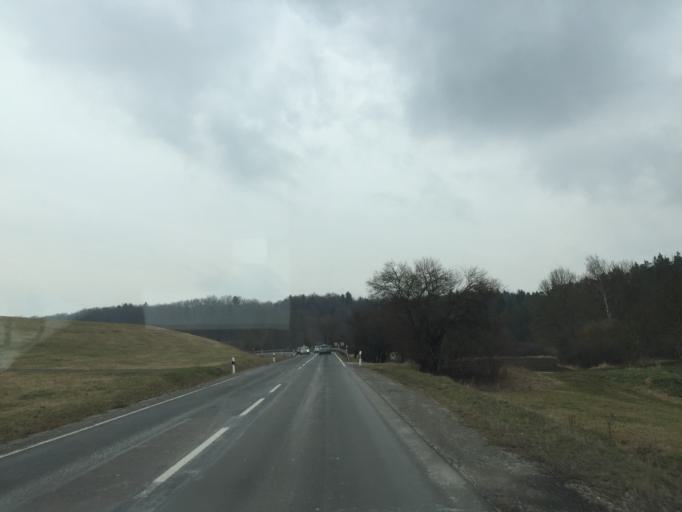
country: DE
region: Thuringia
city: Klettbach
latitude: 50.9082
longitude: 11.1625
